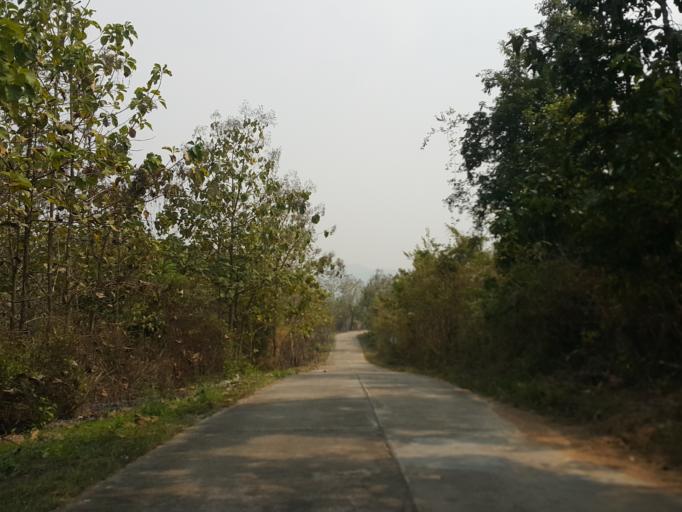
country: TH
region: Lampang
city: Thoen
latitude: 17.6347
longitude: 99.2553
